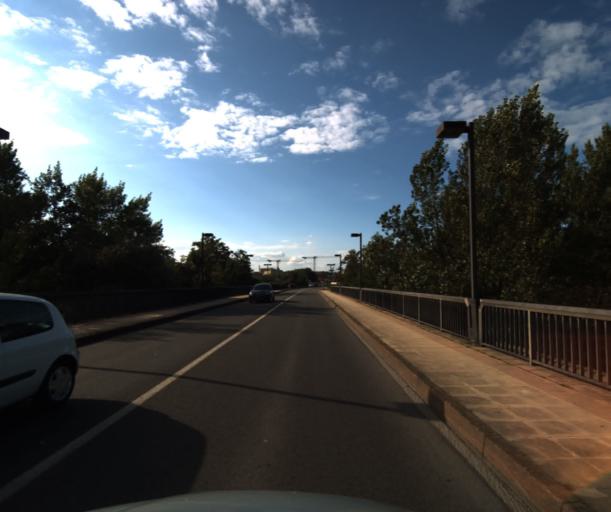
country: FR
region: Midi-Pyrenees
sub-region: Departement de la Haute-Garonne
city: Muret
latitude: 43.4619
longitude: 1.3334
